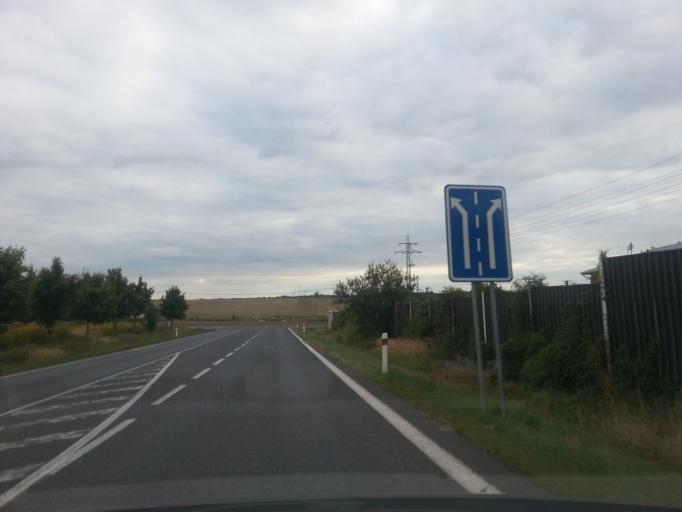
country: CZ
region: Central Bohemia
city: Unhost'
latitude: 50.0868
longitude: 14.1410
